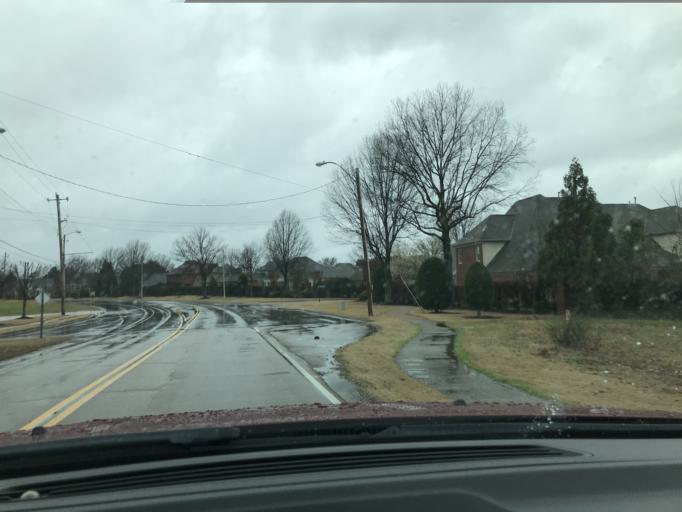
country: US
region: Tennessee
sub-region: Shelby County
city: Collierville
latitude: 35.0539
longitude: -89.6910
